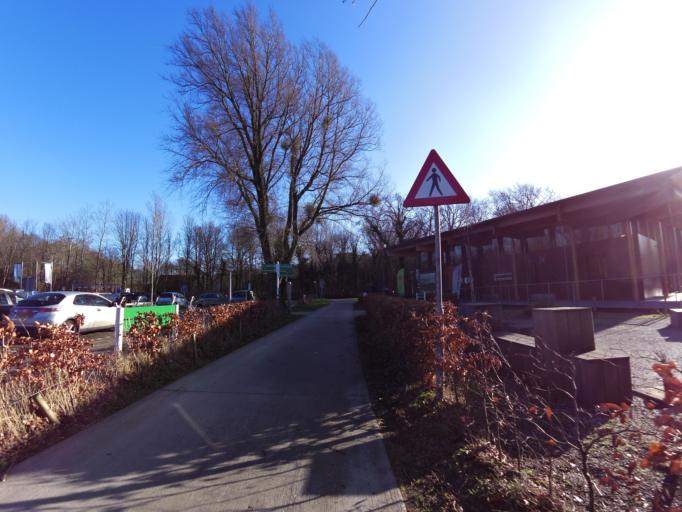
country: NL
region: South Holland
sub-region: Gemeente Hellevoetsluis
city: Nieuw-Helvoet
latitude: 51.9020
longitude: 4.0694
